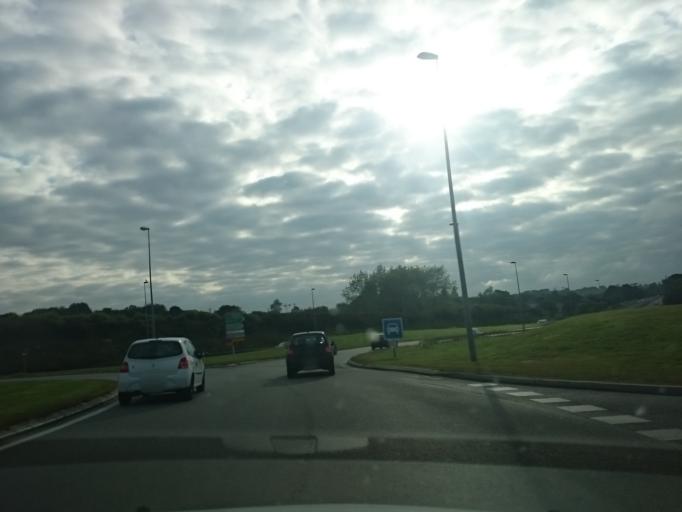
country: FR
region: Brittany
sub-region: Departement du Finistere
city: Gouesnou
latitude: 48.4184
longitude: -4.4391
